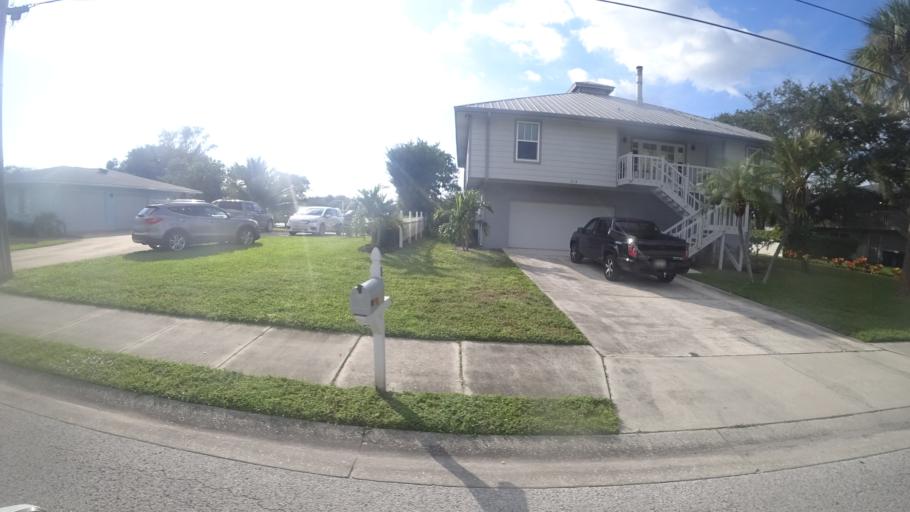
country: US
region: Florida
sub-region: Manatee County
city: Palmetto
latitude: 27.5198
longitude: -82.5893
